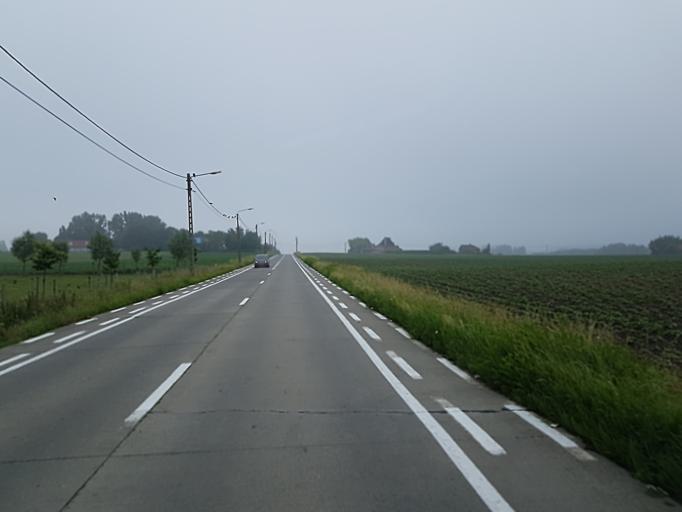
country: BE
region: Wallonia
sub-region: Province du Hainaut
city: Mouscron
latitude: 50.7612
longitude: 3.1925
